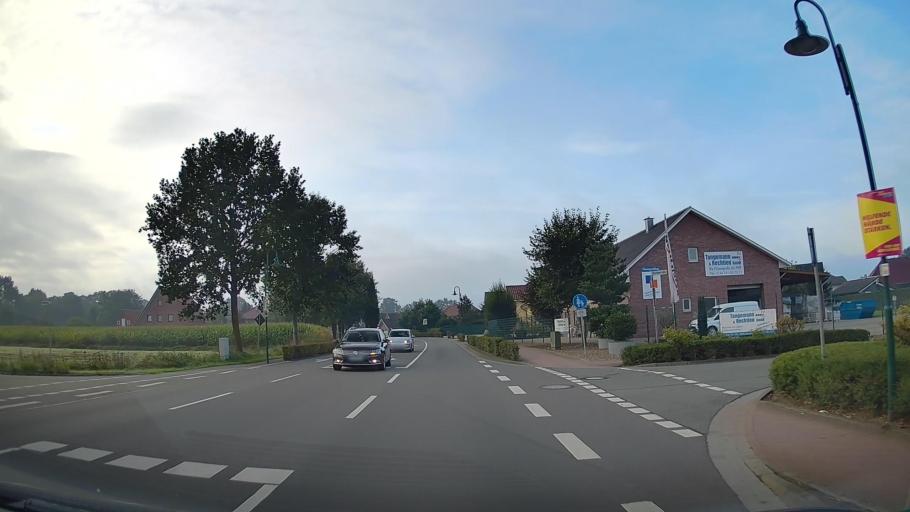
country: DE
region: Lower Saxony
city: Garrel
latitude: 52.9662
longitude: 8.0231
